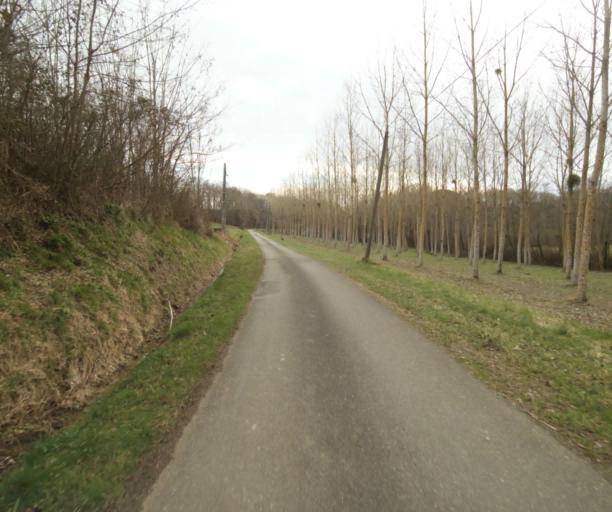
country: FR
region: Midi-Pyrenees
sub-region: Departement du Gers
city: Eauze
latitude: 43.9266
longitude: 0.0622
